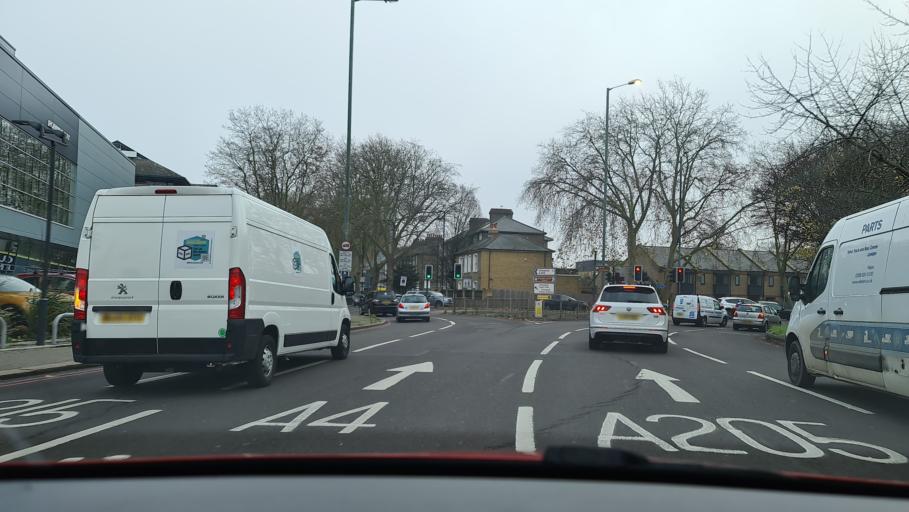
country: GB
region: England
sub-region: Greater London
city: Acton
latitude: 51.4919
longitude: -0.2818
